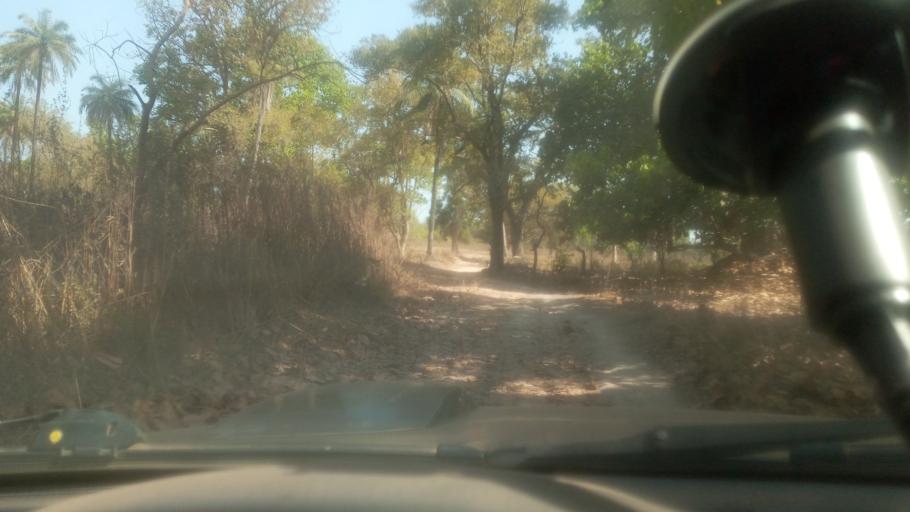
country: GW
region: Oio
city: Farim
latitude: 12.4721
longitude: -15.4062
